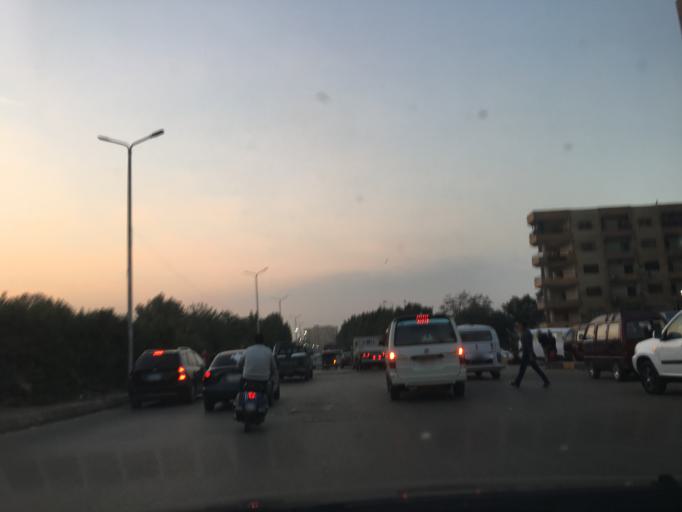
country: EG
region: Al Jizah
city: Al Jizah
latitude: 29.9900
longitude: 31.1350
